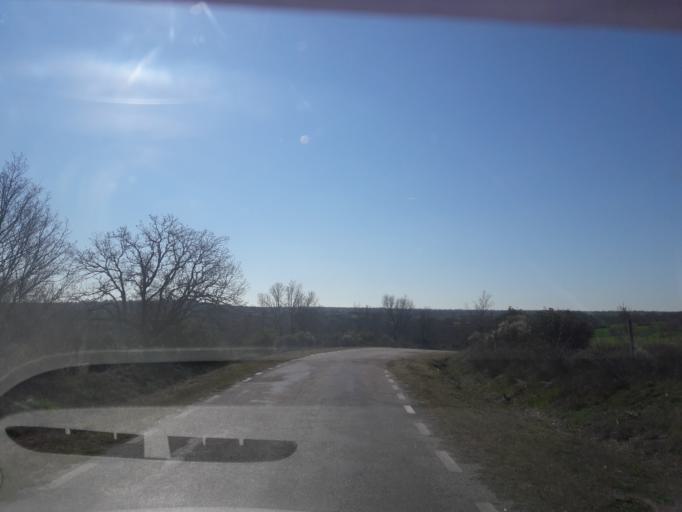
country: ES
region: Castille and Leon
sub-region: Provincia de Salamanca
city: Valsalabroso
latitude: 41.1638
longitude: -6.4979
